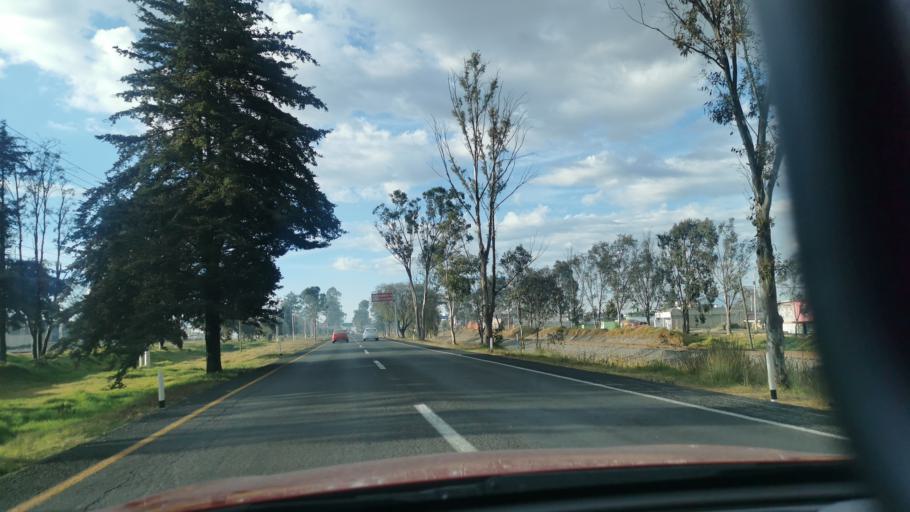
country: MX
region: Mexico
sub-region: Toluca
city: Colonia Aviacion Autopan
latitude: 19.3759
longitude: -99.7001
